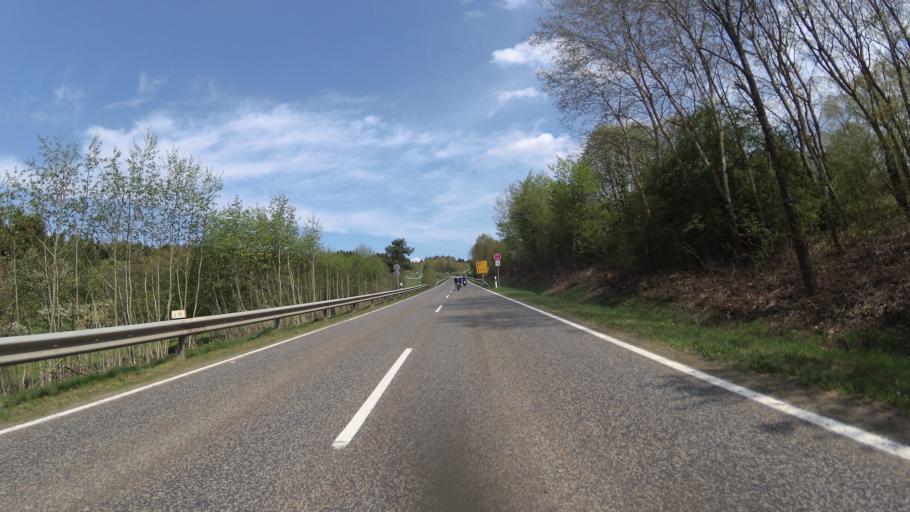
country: DE
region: Rheinland-Pfalz
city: Mullenbach
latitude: 50.3237
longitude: 6.9218
